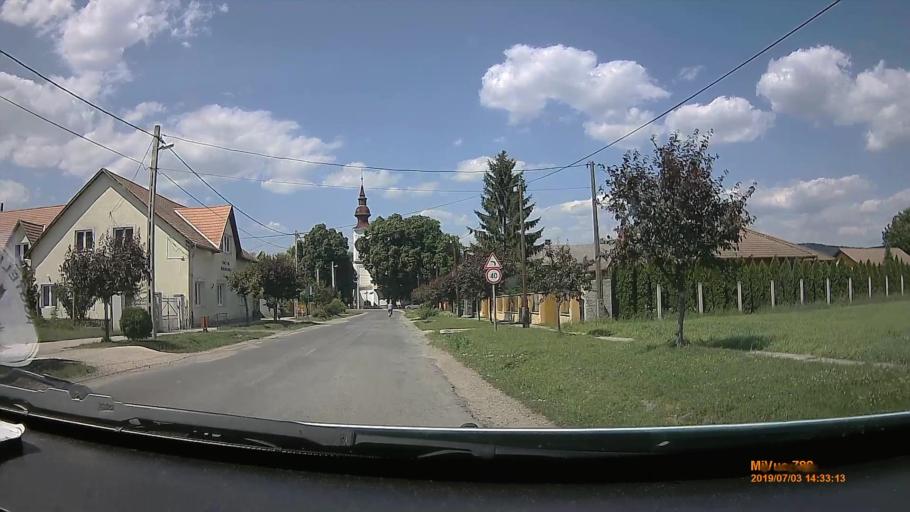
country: HU
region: Borsod-Abauj-Zemplen
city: Putnok
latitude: 48.2728
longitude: 20.4623
